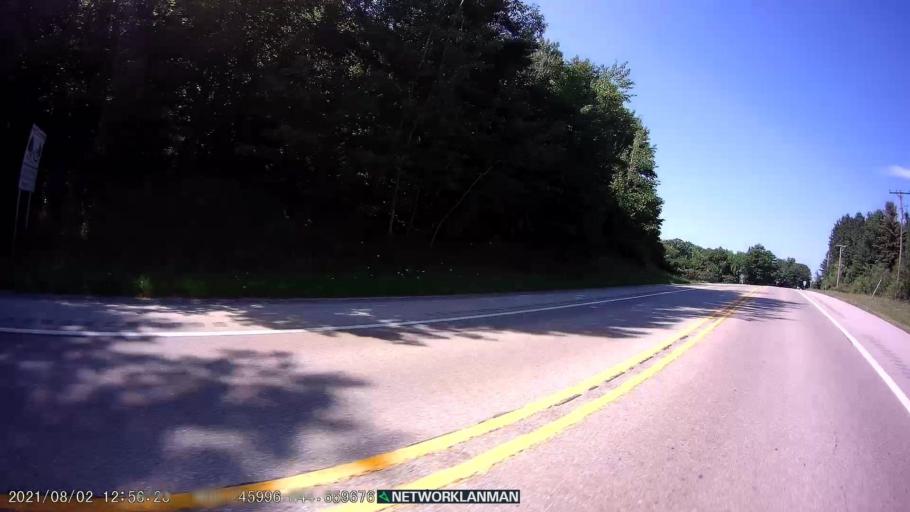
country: US
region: Michigan
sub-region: Benzie County
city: Frankfort
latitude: 44.6599
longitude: -86.2460
